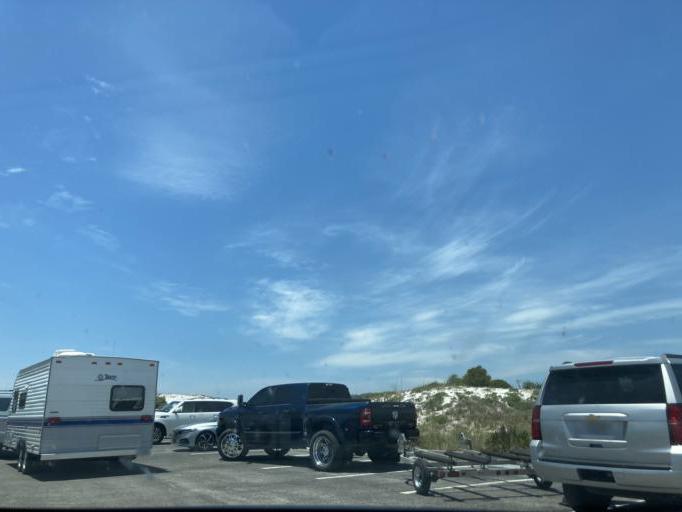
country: US
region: Florida
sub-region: Bay County
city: Lower Grand Lagoon
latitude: 30.1262
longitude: -85.7351
